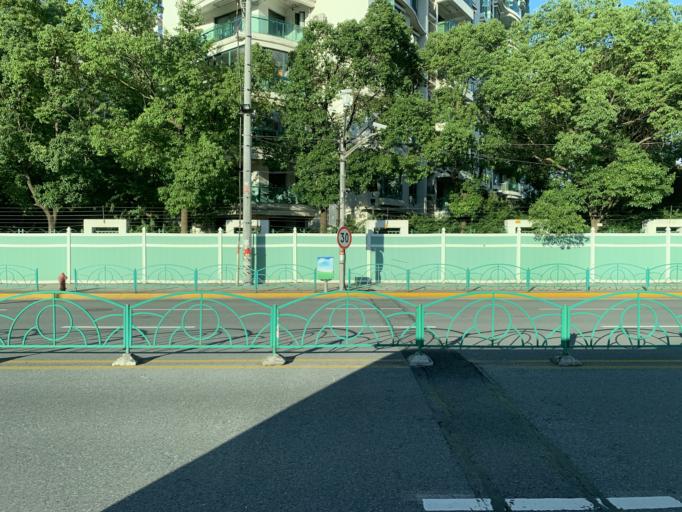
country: CN
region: Shanghai Shi
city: Huamu
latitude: 31.2233
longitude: 121.5471
